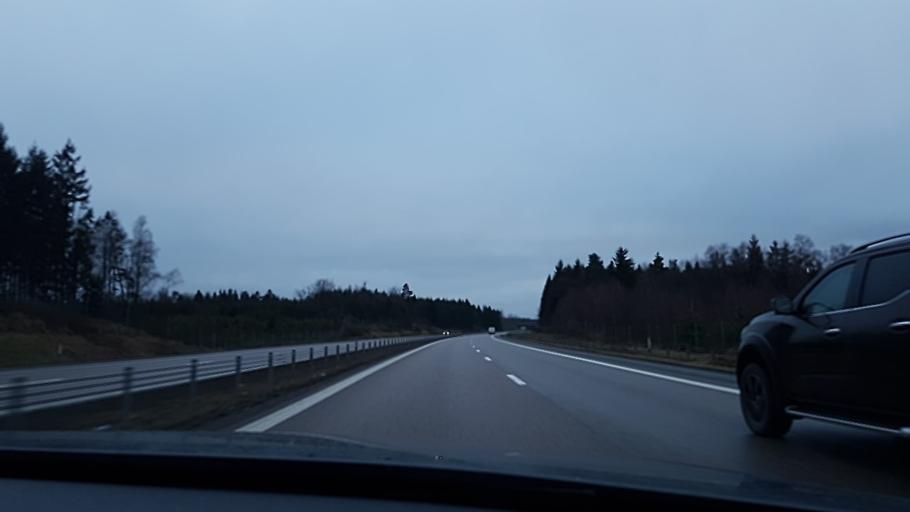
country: SE
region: Skane
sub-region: Orkelljunga Kommun
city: OErkelljunga
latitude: 56.2709
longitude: 13.3261
